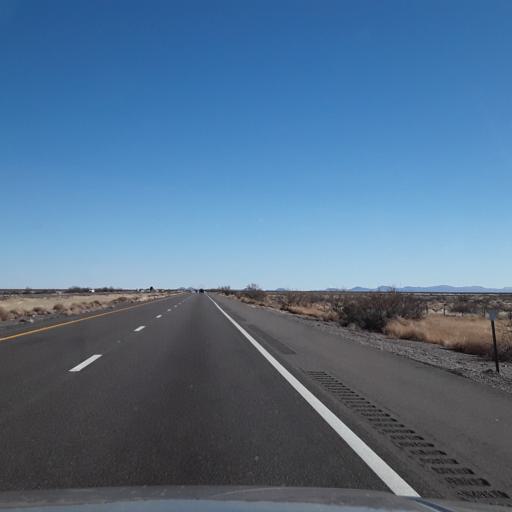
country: US
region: New Mexico
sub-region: Luna County
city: Deming
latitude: 32.2720
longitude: -107.5394
